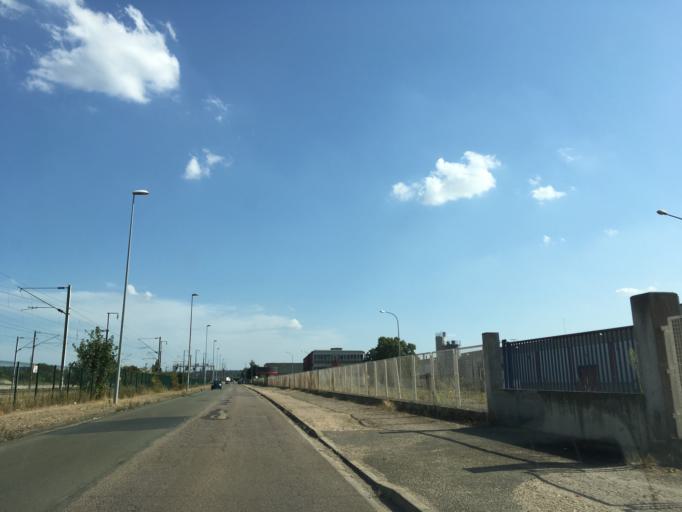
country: FR
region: Haute-Normandie
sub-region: Departement de l'Eure
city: Vernon
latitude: 49.1012
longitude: 1.4635
